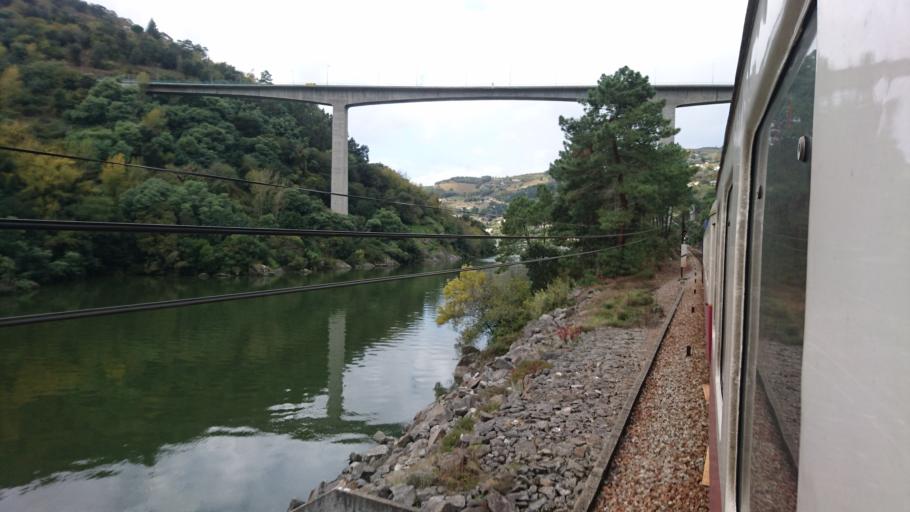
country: PT
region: Viseu
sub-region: Resende
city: Resende
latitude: 41.1214
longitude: -7.9373
